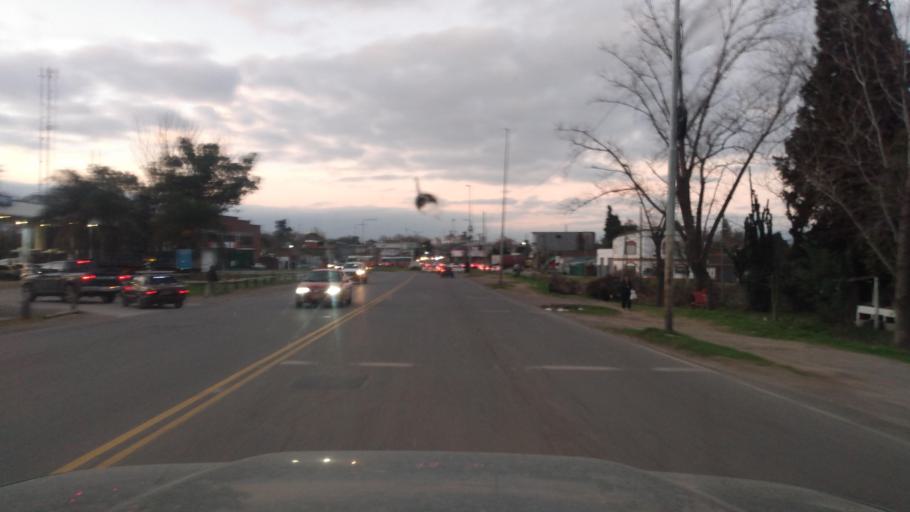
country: AR
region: Buenos Aires
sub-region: Partido de Pilar
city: Pilar
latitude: -34.4687
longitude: -58.9170
